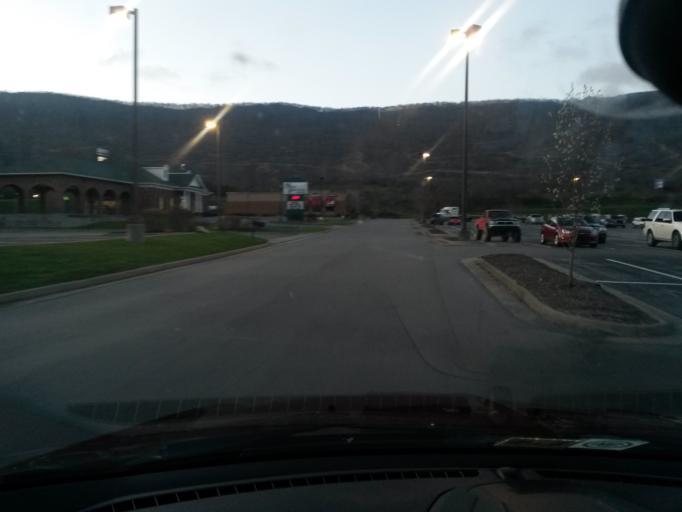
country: US
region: Virginia
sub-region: Tazewell County
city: Bluefield
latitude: 37.2391
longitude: -81.2502
